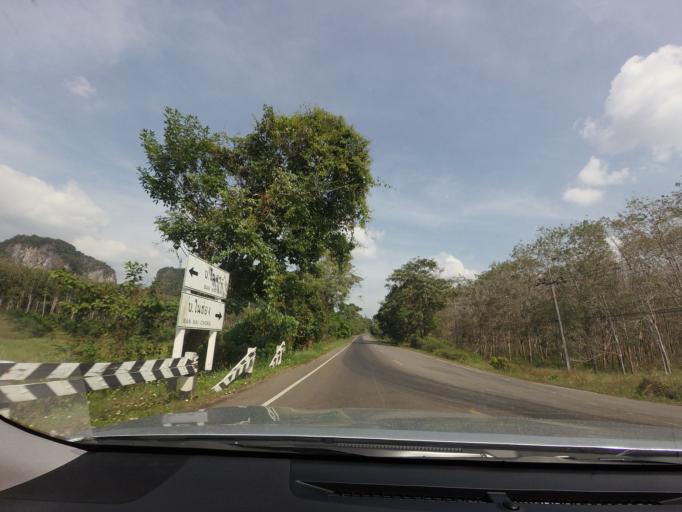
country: TH
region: Phangnga
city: Ban Ao Nang
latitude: 8.1432
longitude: 98.8334
